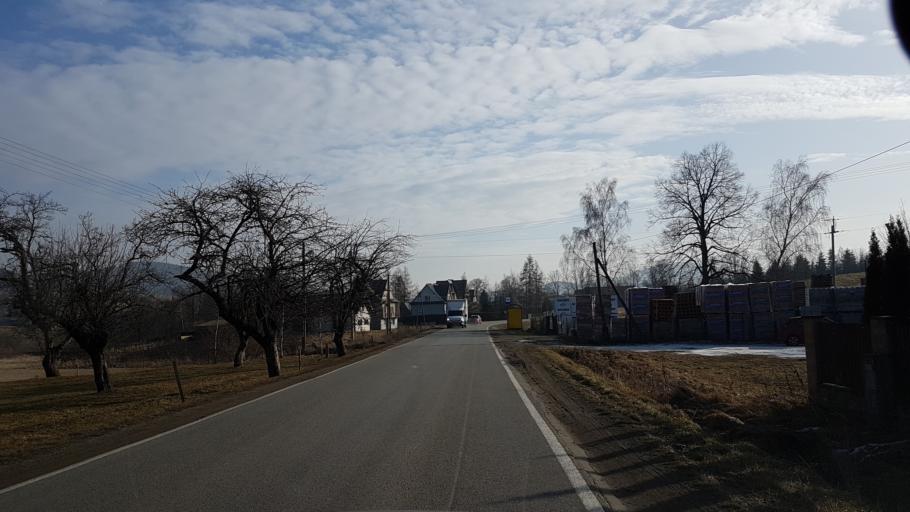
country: PL
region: Lesser Poland Voivodeship
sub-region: Powiat limanowski
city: Lukowica
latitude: 49.6514
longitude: 20.4992
